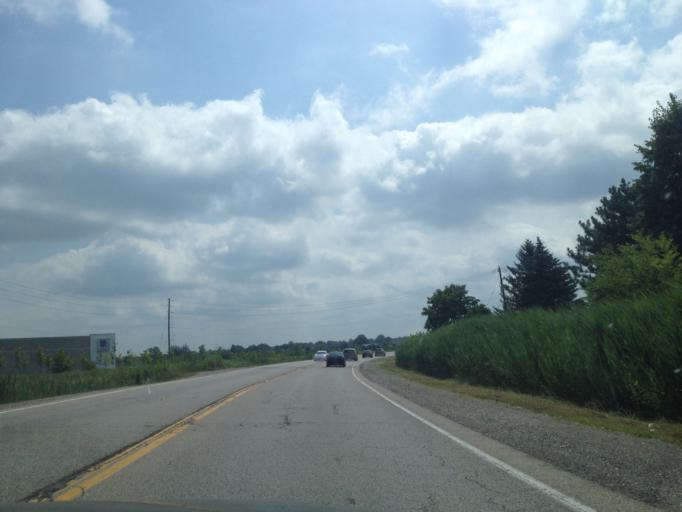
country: CA
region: Ontario
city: London
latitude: 43.0268
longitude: -81.1658
